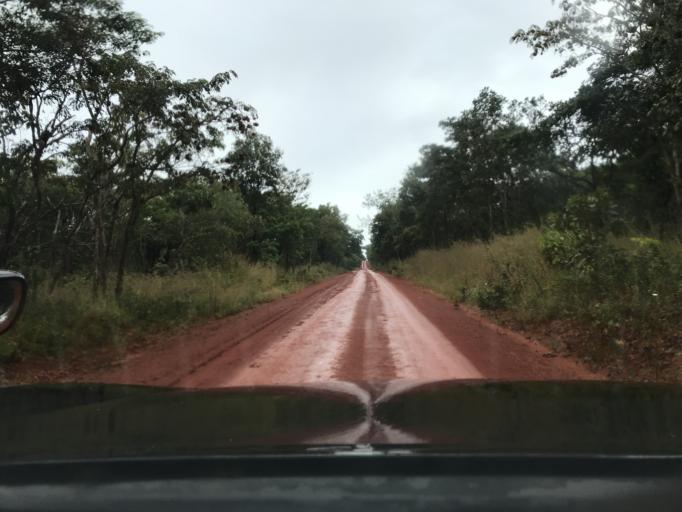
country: TZ
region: Kigoma
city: Uvinza
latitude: -5.2955
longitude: 30.3729
